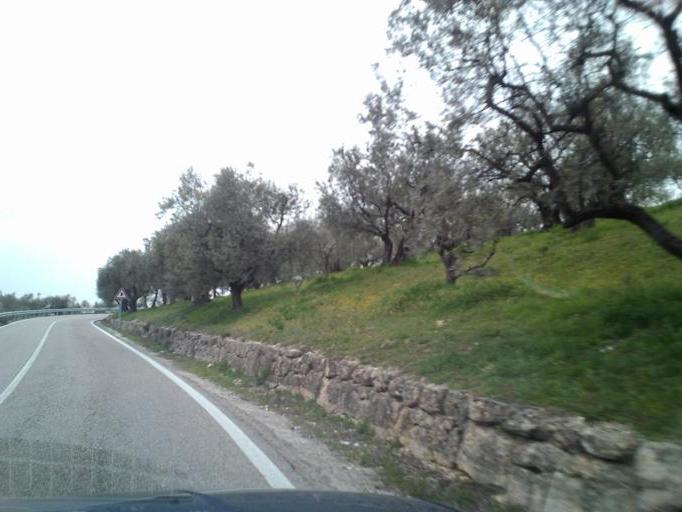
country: IT
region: Veneto
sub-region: Provincia di Verona
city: Montorio
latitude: 45.4910
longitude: 11.0788
